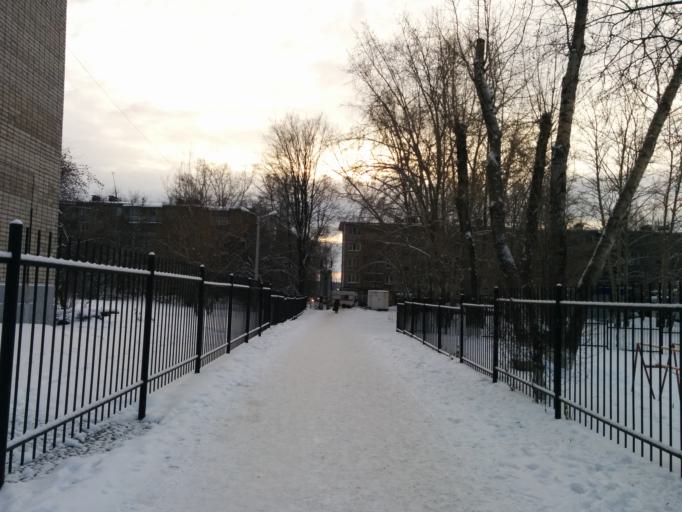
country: RU
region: Perm
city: Perm
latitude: 57.9808
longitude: 56.2923
